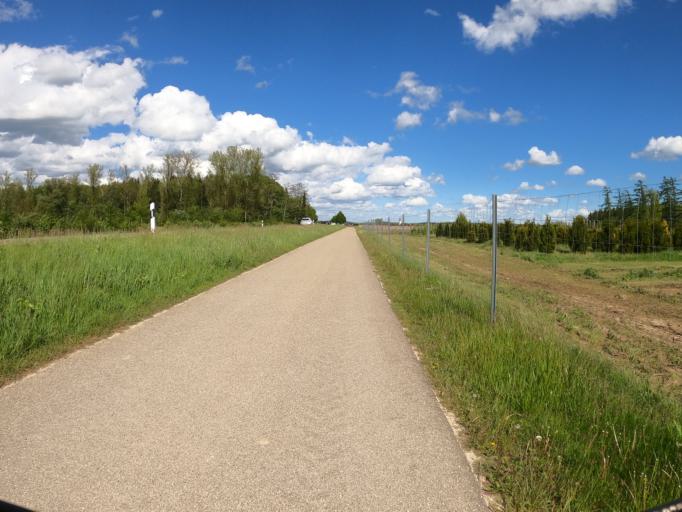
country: DE
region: Bavaria
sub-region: Swabia
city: Leipheim
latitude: 48.4318
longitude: 10.2298
